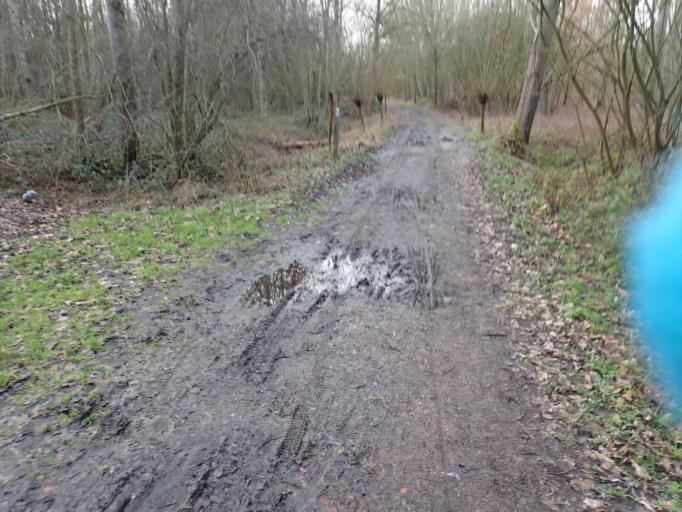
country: BE
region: Flanders
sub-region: Provincie Vlaams-Brabant
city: Tremelo
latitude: 50.9810
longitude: 4.6980
